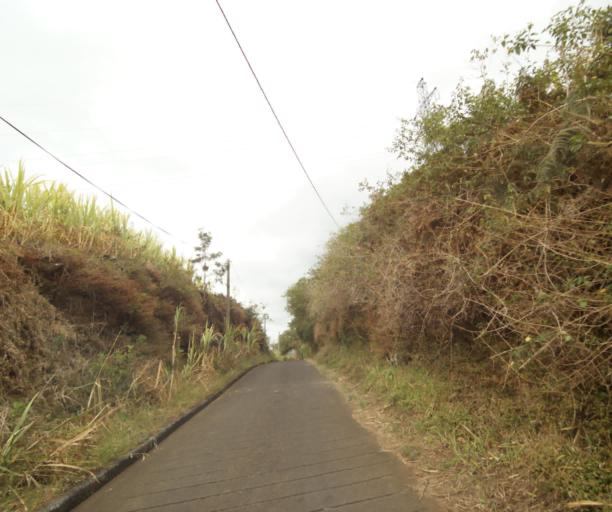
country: RE
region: Reunion
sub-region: Reunion
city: Saint-Paul
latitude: -21.0300
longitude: 55.3160
